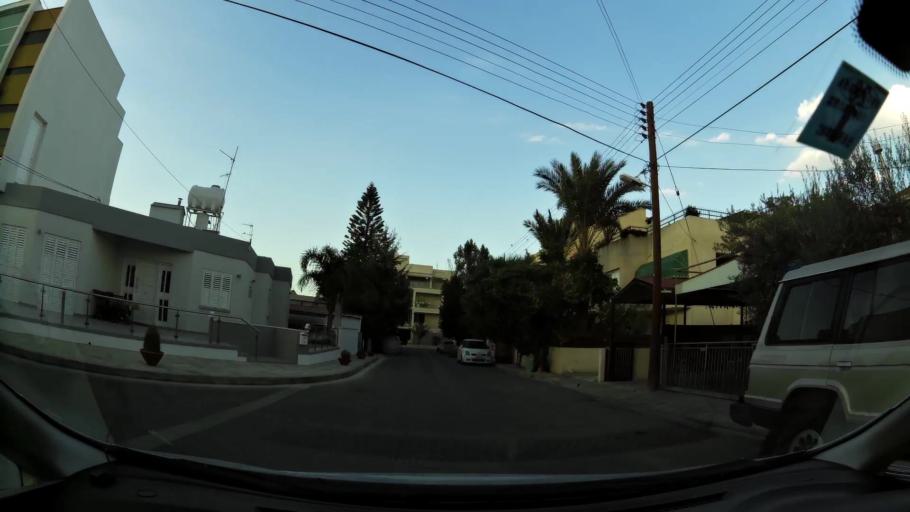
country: CY
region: Lefkosia
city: Nicosia
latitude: 35.1329
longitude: 33.3323
